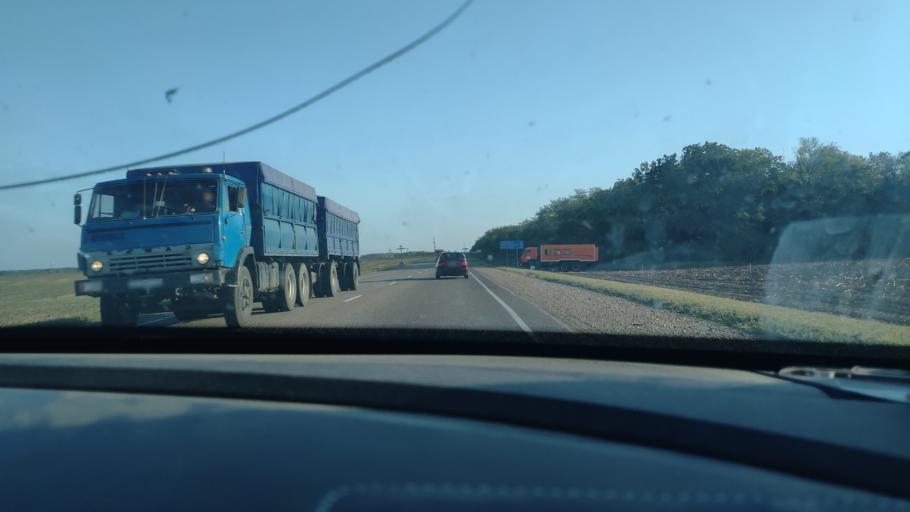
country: RU
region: Krasnodarskiy
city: Novominskaya
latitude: 46.3041
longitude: 38.9314
